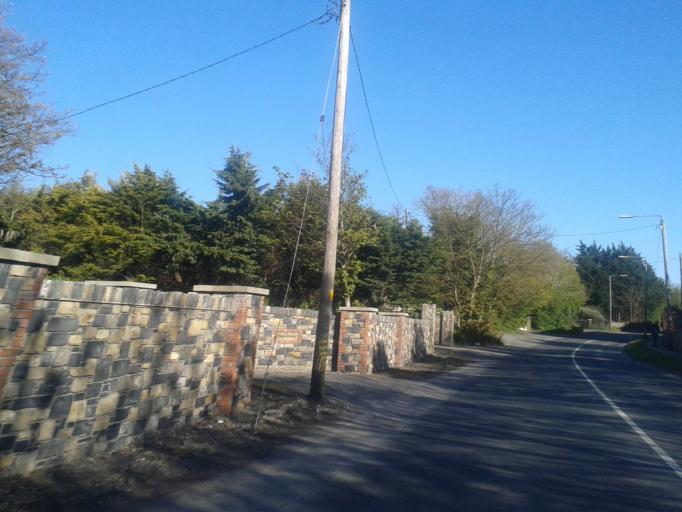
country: IE
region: Leinster
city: Kinsealy-Drinan
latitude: 53.4446
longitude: -6.1969
